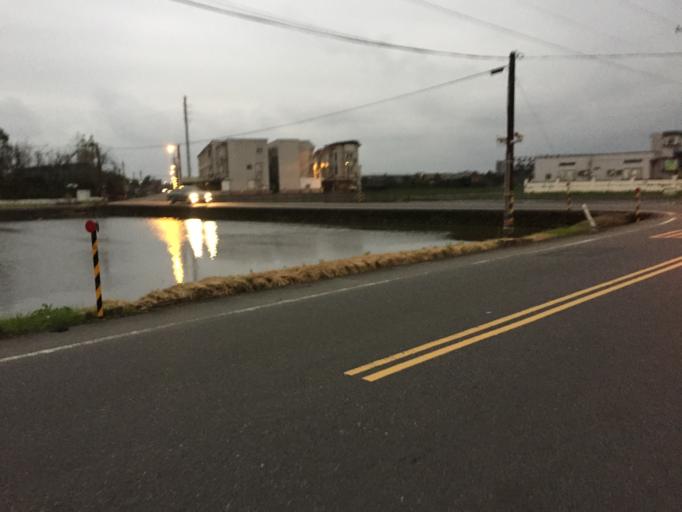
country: TW
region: Taiwan
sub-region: Yilan
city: Yilan
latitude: 24.6610
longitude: 121.7781
